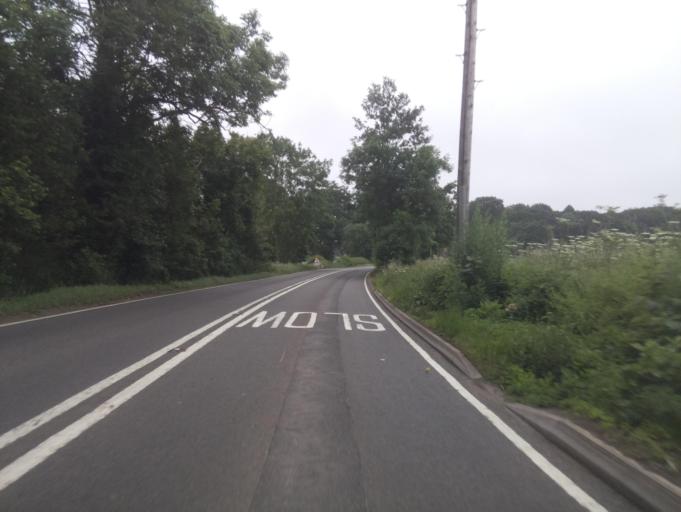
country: GB
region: England
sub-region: Derbyshire
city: Netherseal
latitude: 52.7018
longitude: -1.5546
